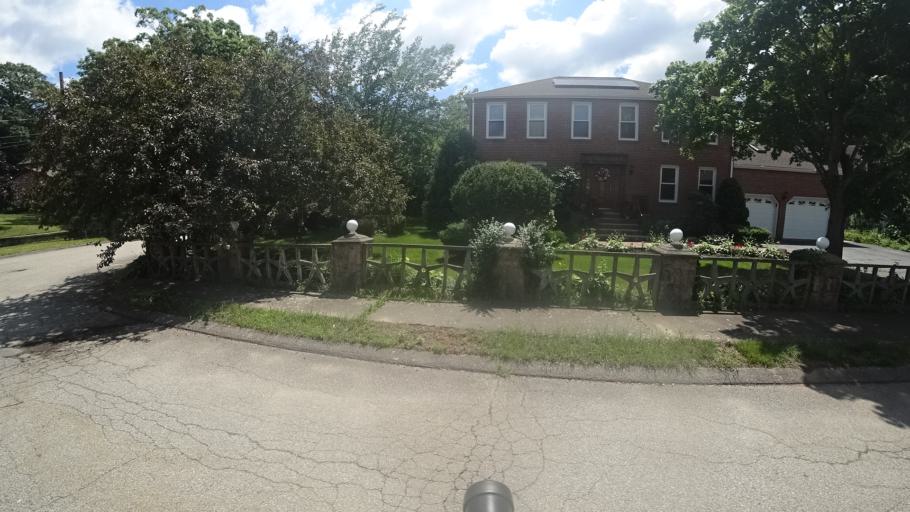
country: US
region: Massachusetts
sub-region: Norfolk County
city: Dedham
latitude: 42.2538
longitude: -71.1587
